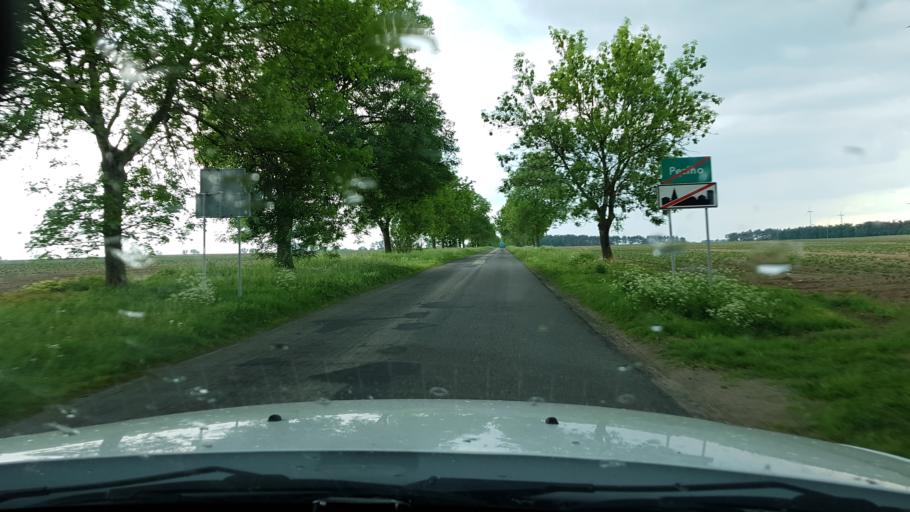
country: PL
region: West Pomeranian Voivodeship
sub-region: Powiat stargardzki
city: Marianowo
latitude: 53.3340
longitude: 15.1917
